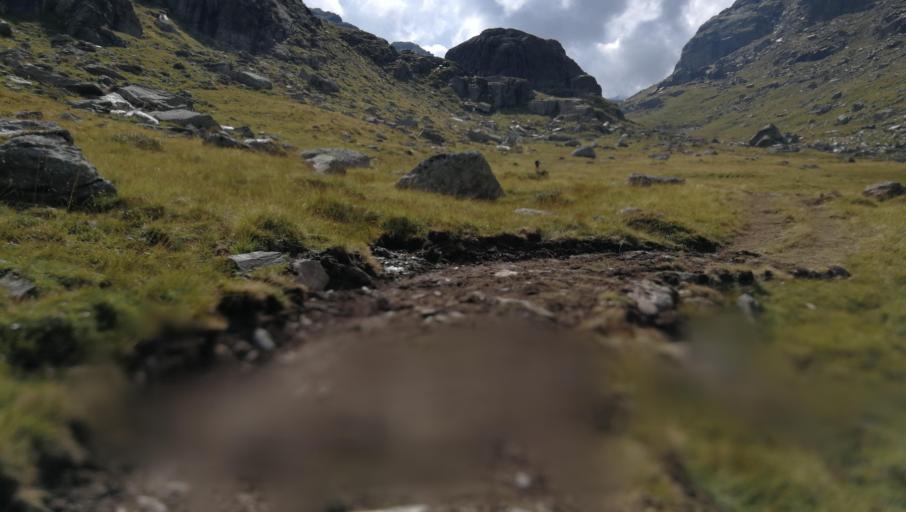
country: CH
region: Grisons
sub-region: Bernina District
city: Poschiavo
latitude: 46.3120
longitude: 9.9802
